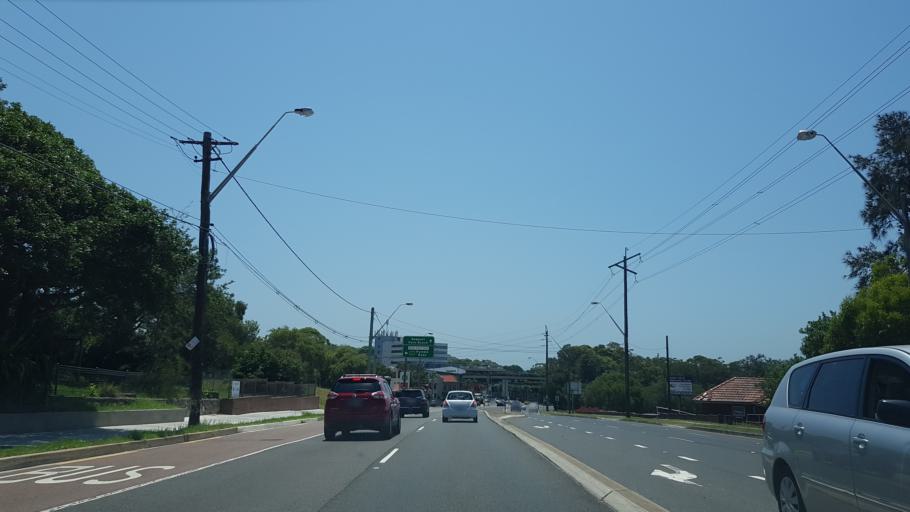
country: AU
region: New South Wales
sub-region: Pittwater
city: Warriewood
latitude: -33.6818
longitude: 151.3031
